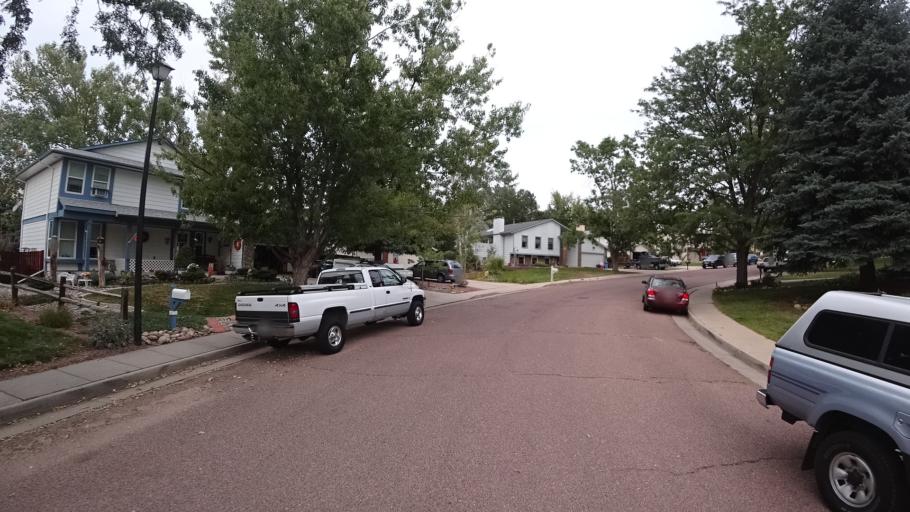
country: US
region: Colorado
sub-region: El Paso County
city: Cimarron Hills
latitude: 38.9040
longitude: -104.7352
